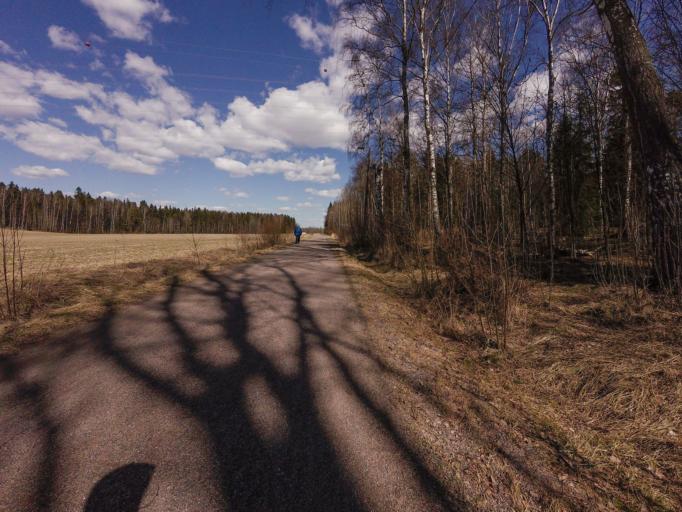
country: FI
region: Uusimaa
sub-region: Helsinki
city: Vantaa
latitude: 60.2130
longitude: 25.0298
